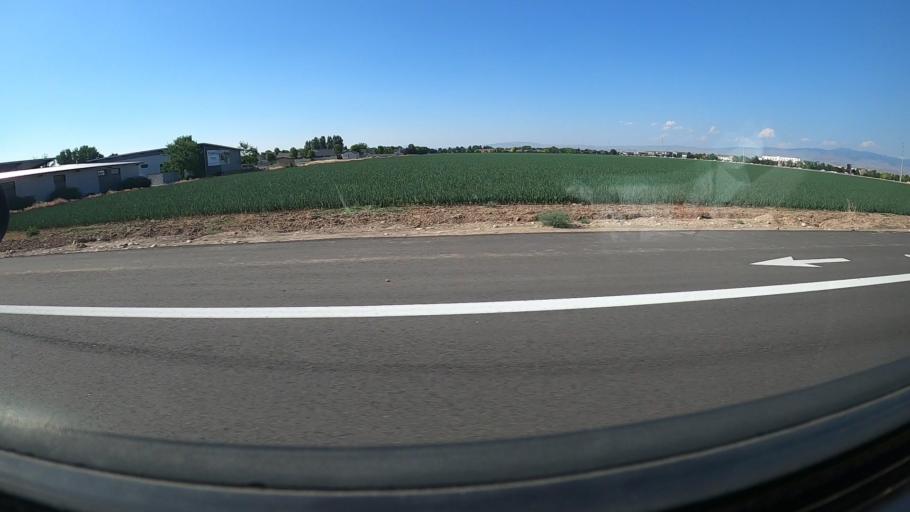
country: US
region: Idaho
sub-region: Ada County
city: Meridian
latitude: 43.6194
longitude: -116.3586
